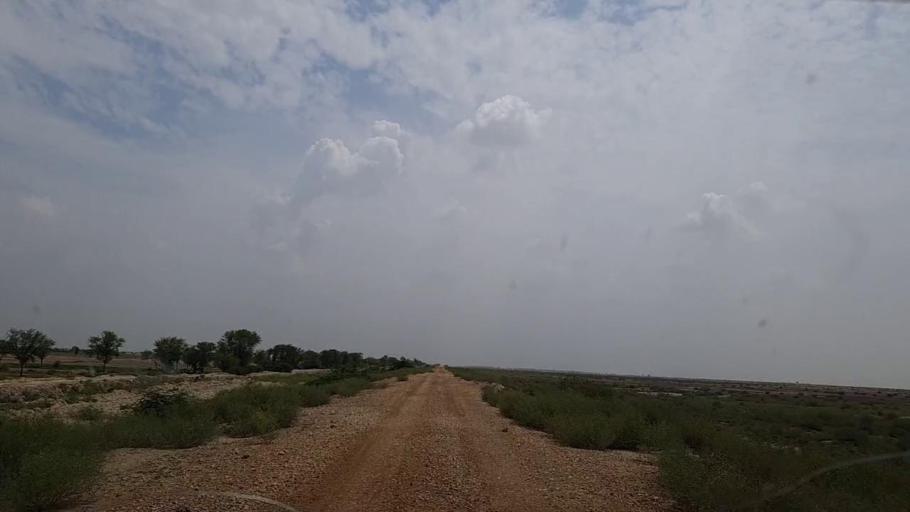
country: PK
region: Sindh
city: Johi
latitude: 26.8010
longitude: 67.6030
